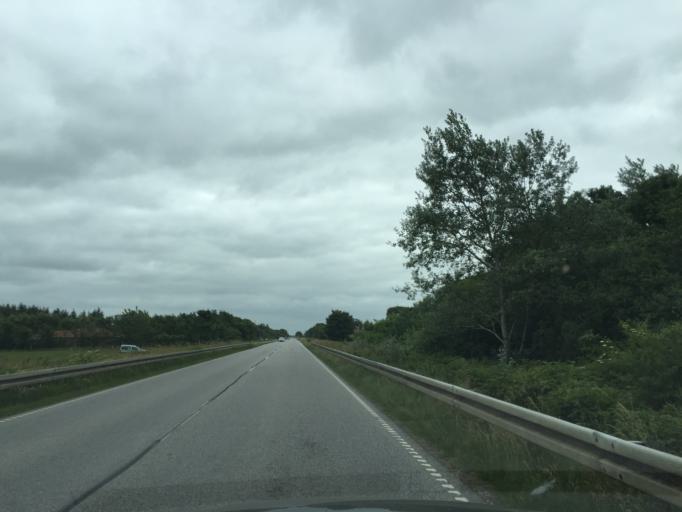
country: DK
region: South Denmark
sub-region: Tonder Kommune
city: Sherrebek
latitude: 55.2384
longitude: 8.7239
